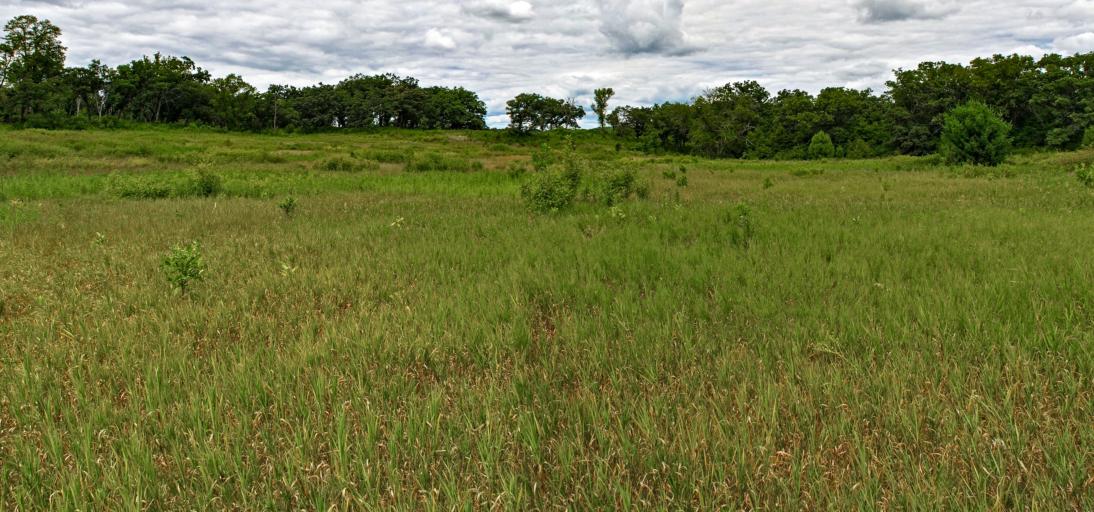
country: US
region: Wisconsin
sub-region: Polk County
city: Osceola
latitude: 45.2893
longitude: -92.7427
